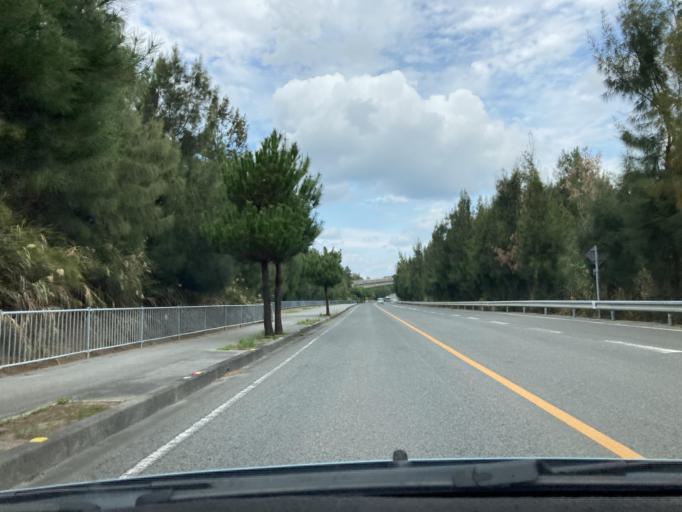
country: JP
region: Okinawa
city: Ishikawa
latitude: 26.4549
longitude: 127.8216
